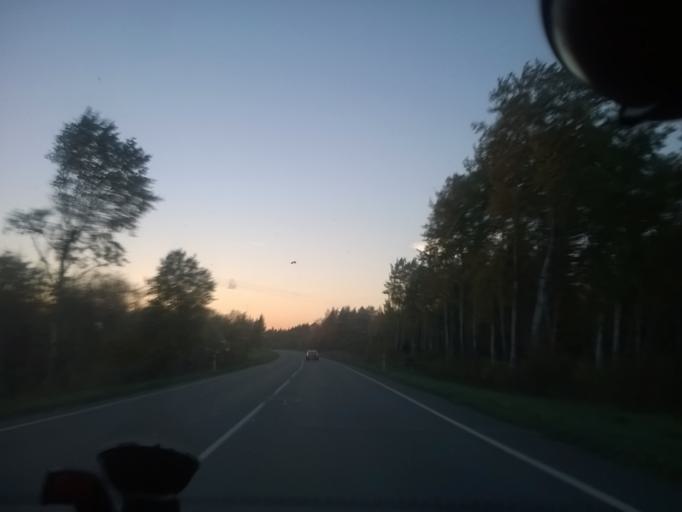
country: EE
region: Laeaene
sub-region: Ridala Parish
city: Uuemoisa
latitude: 58.9614
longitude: 23.6914
